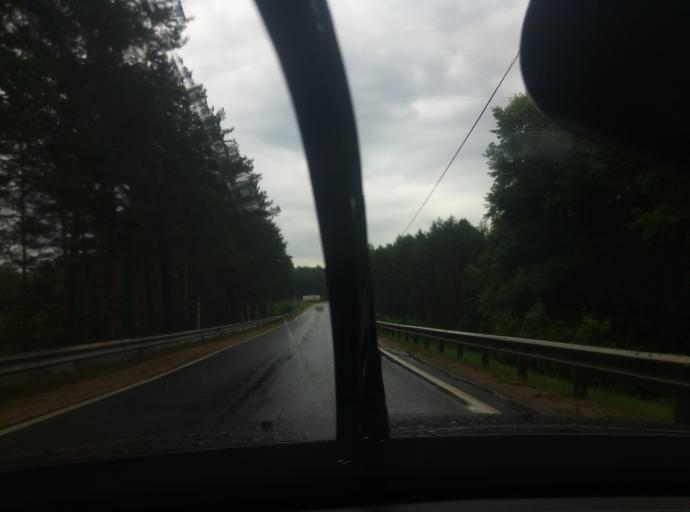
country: RU
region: Moskovskaya
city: Danki
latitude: 54.9062
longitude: 37.5088
